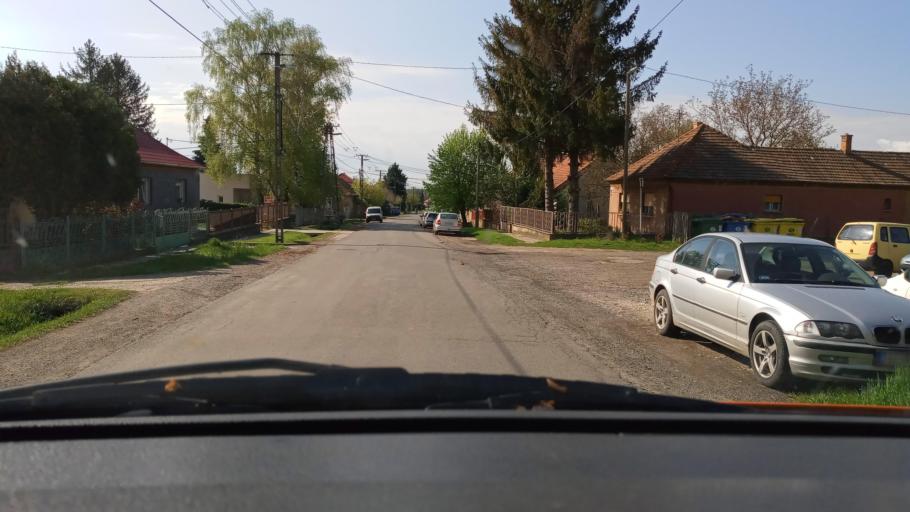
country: HU
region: Baranya
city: Hosszuheteny
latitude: 46.1175
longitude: 18.3407
